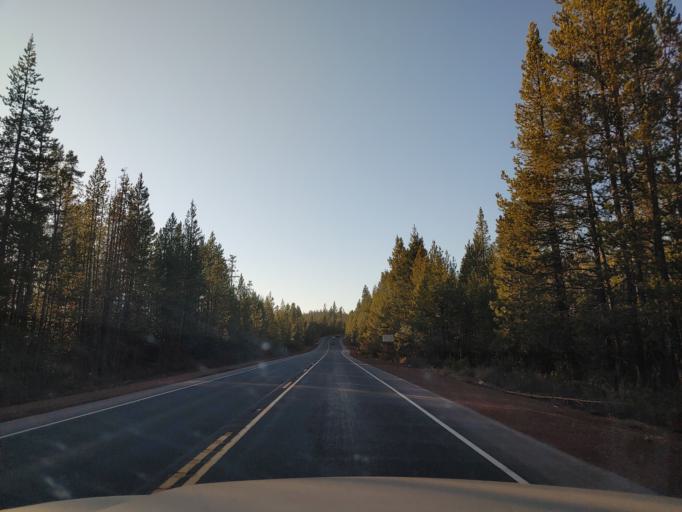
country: US
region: Oregon
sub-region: Deschutes County
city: La Pine
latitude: 43.4407
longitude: -121.8655
